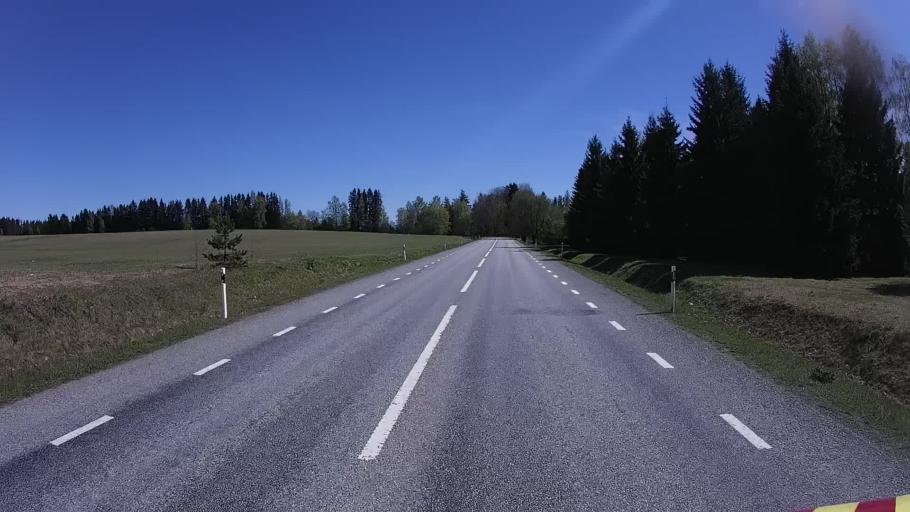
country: EE
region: Laeaene-Virumaa
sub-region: Tapa vald
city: Tapa
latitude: 59.2498
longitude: 25.6799
